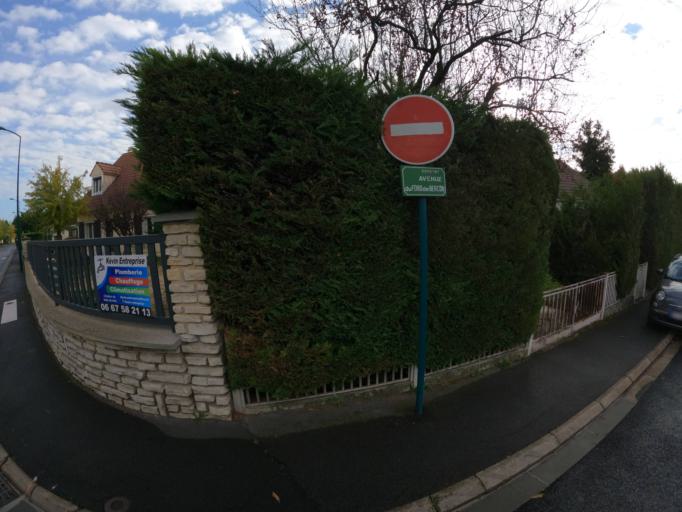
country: FR
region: Ile-de-France
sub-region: Departement de Seine-et-Marne
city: Courtry
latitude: 48.9127
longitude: 2.6011
